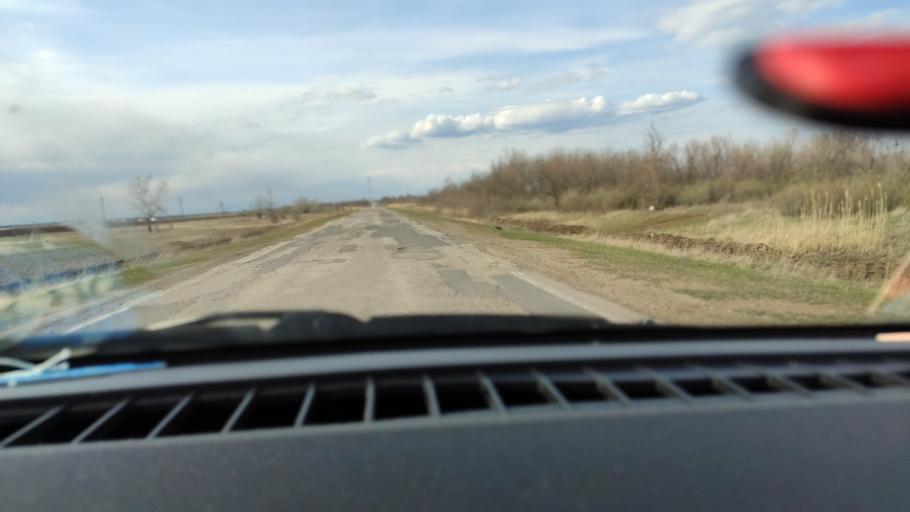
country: RU
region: Saratov
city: Rovnoye
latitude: 51.0105
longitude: 46.0986
